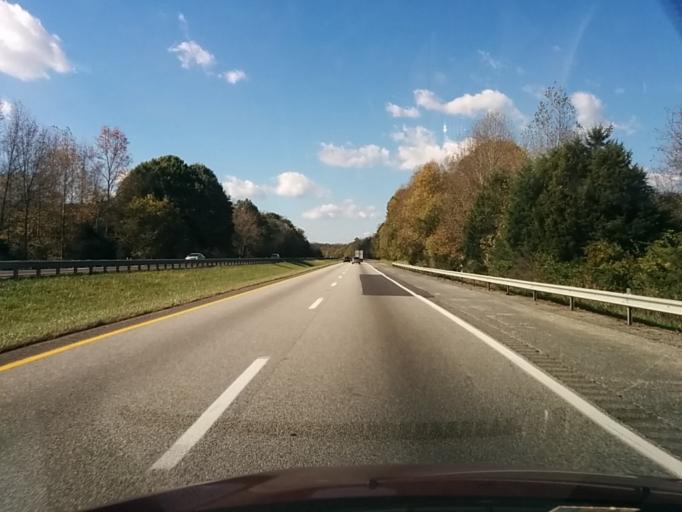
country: US
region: Virginia
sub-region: Botetourt County
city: Buchanan
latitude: 37.5196
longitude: -79.7212
